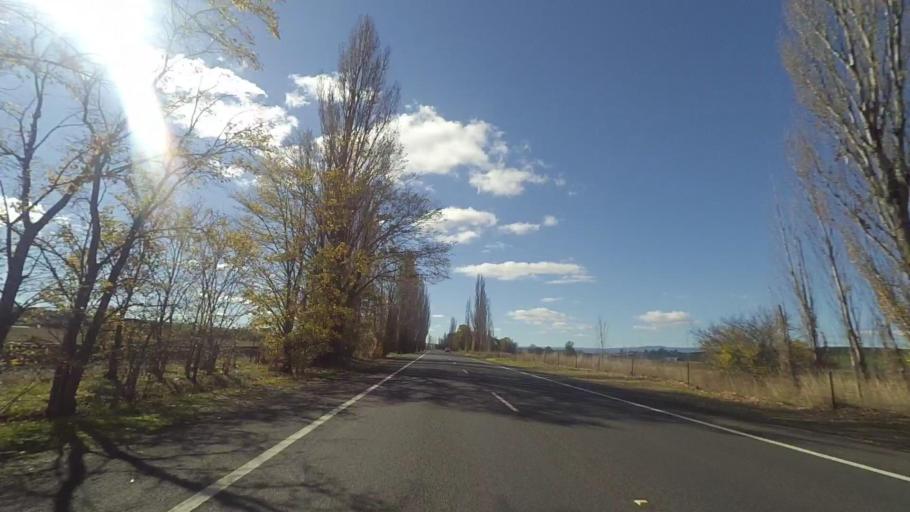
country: AU
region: New South Wales
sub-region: Bathurst Regional
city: Perthville
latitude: -33.4579
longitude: 149.5742
